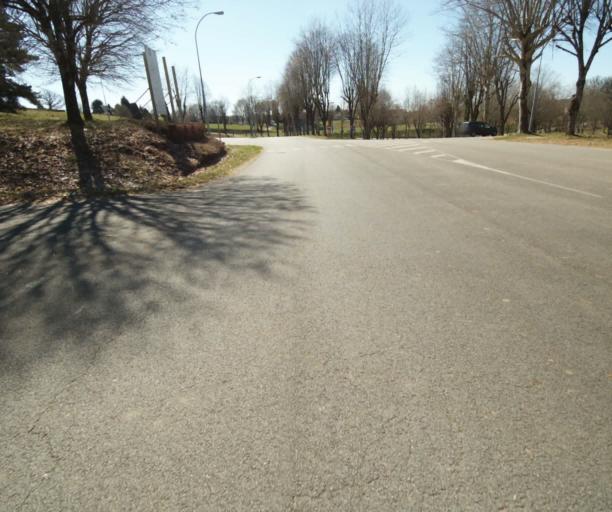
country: FR
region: Limousin
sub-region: Departement de la Correze
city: Seilhac
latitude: 45.3771
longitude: 1.6999
